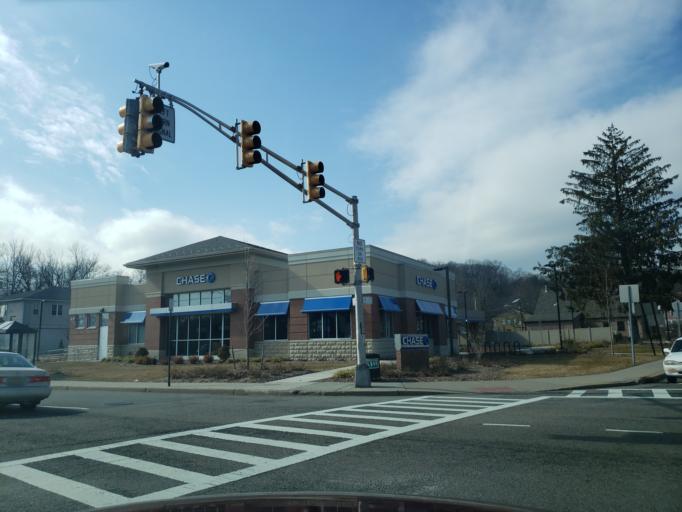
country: US
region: New Jersey
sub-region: Essex County
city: West Orange
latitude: 40.8102
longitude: -74.2605
